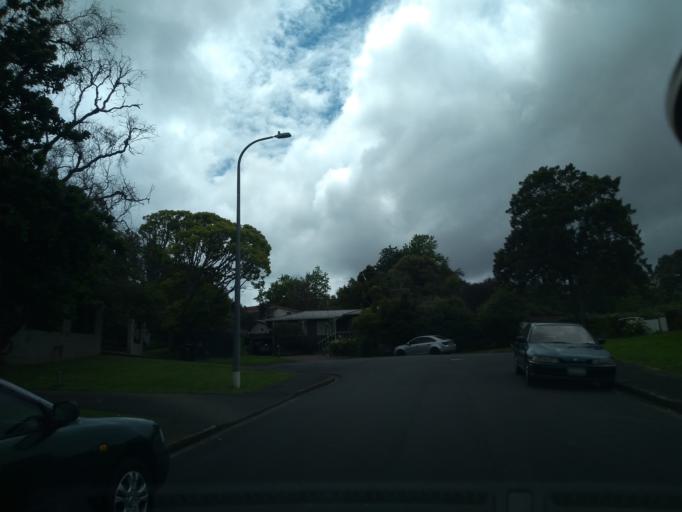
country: NZ
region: Auckland
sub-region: Auckland
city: Tamaki
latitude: -36.9118
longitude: 174.8264
